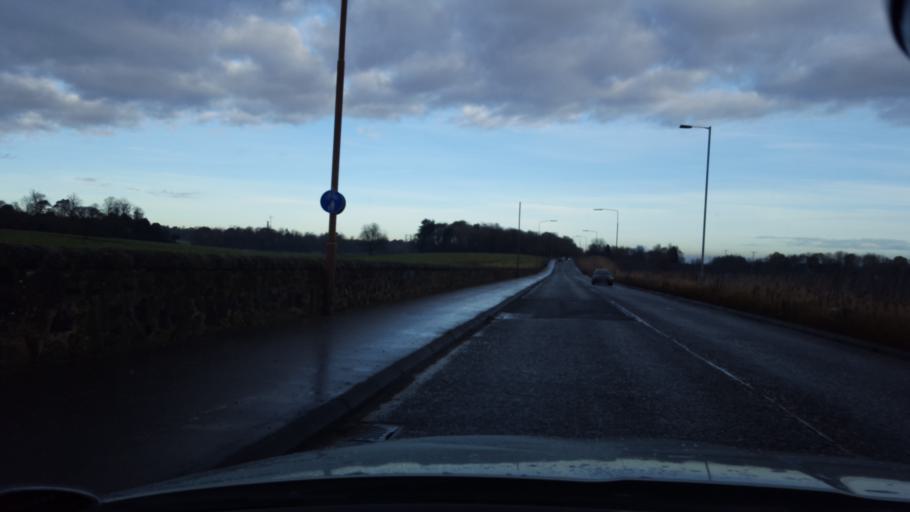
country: GB
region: Scotland
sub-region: Edinburgh
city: Kirkliston
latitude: 55.9682
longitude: -3.4013
